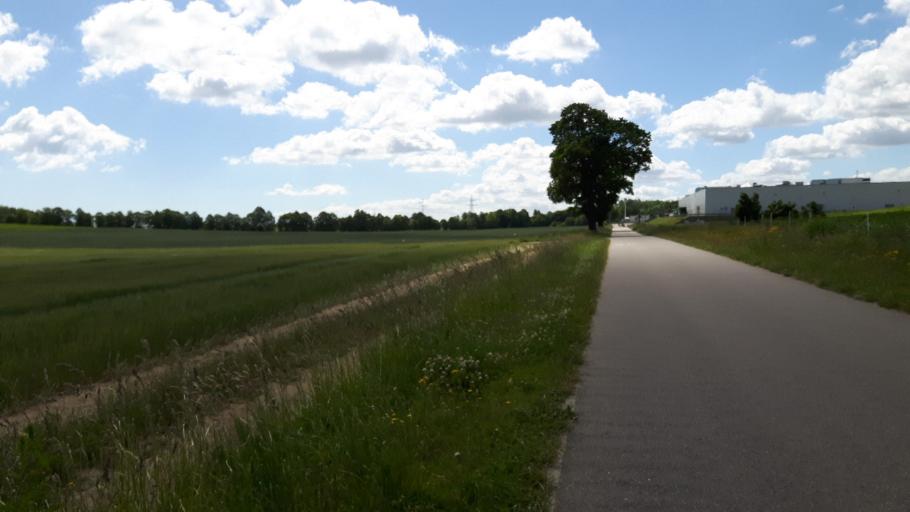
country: PL
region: Pomeranian Voivodeship
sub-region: Gdynia
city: Pogorze
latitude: 54.5681
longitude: 18.5033
